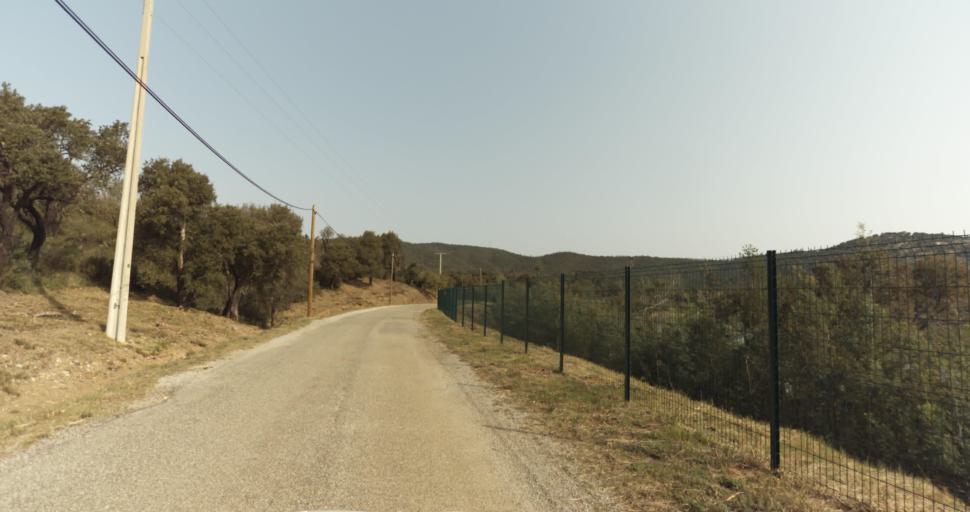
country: FR
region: Provence-Alpes-Cote d'Azur
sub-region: Departement du Var
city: Bormes-les-Mimosas
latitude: 43.1460
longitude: 6.2929
